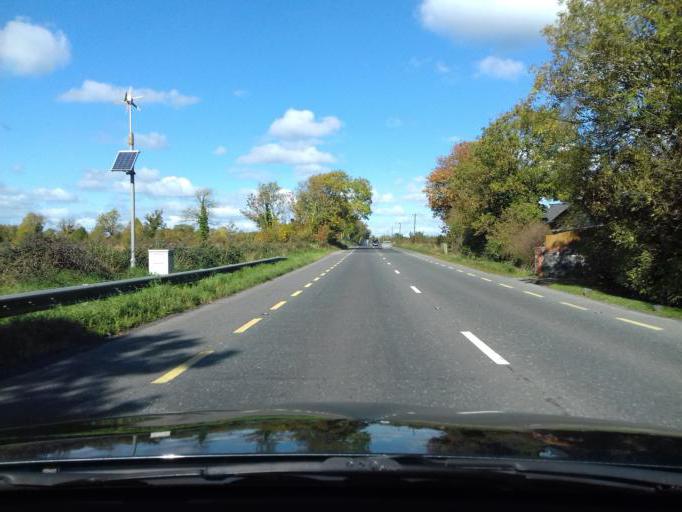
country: IE
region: Leinster
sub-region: An Mhi
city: Ashbourne
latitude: 53.5418
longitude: -6.4280
